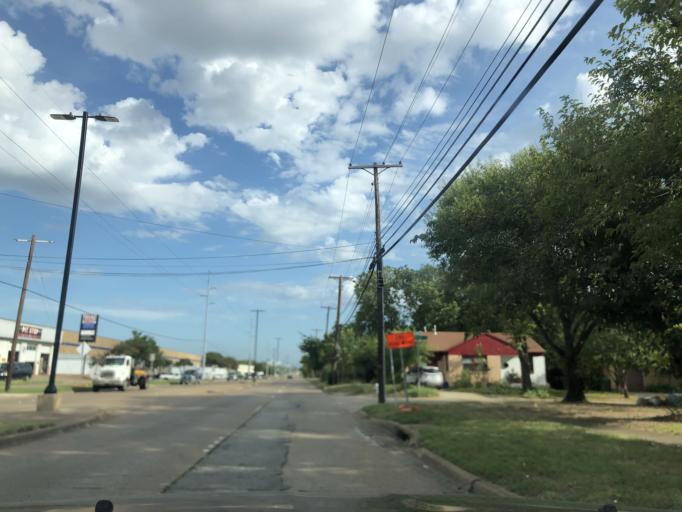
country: US
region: Texas
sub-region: Dallas County
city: Garland
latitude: 32.8803
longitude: -96.6655
